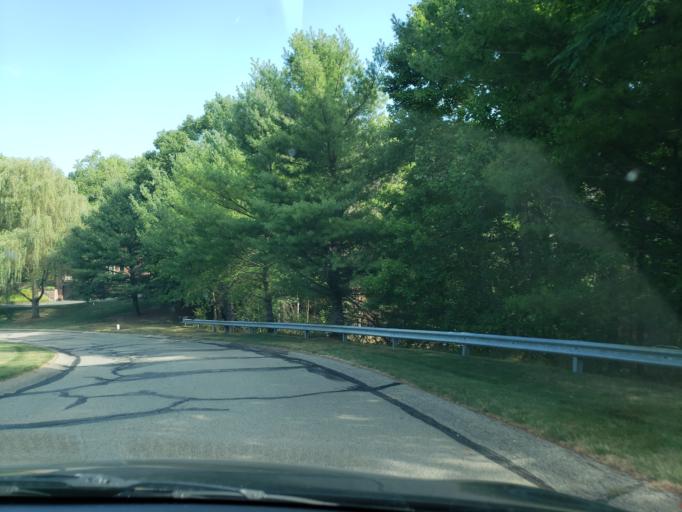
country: US
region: Pennsylvania
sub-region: Allegheny County
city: Coraopolis
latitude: 40.5401
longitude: -80.1480
